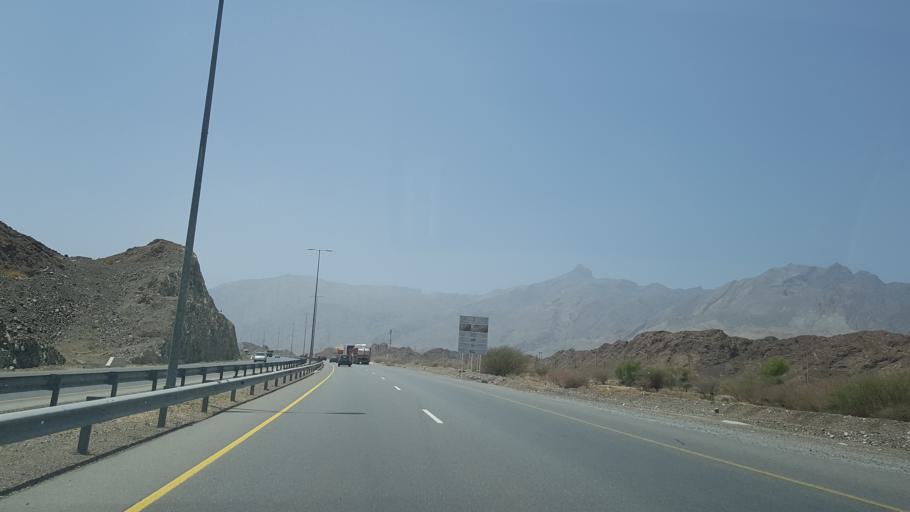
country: OM
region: Muhafazat ad Dakhiliyah
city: Sufalat Sama'il
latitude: 23.3370
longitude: 57.9888
